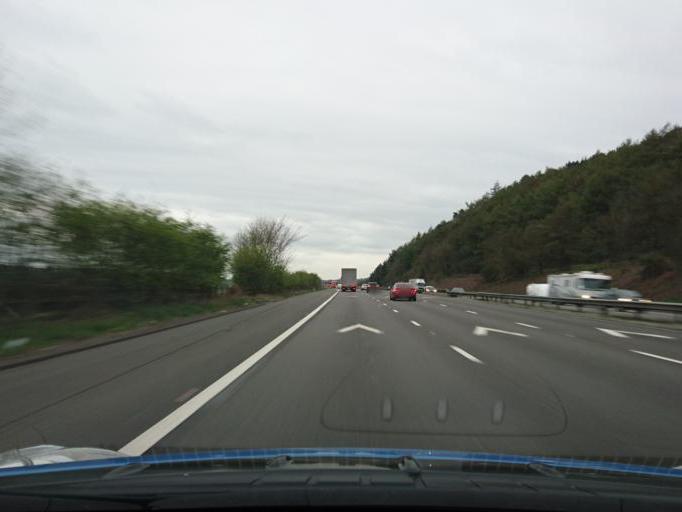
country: GB
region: England
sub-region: Staffordshire
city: Barlaston
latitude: 52.9405
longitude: -2.2156
